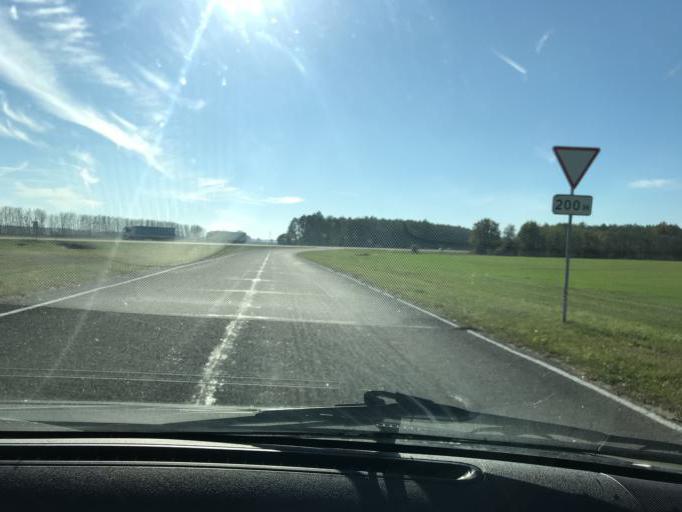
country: BY
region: Brest
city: Ivatsevichy
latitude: 52.6995
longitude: 25.3599
